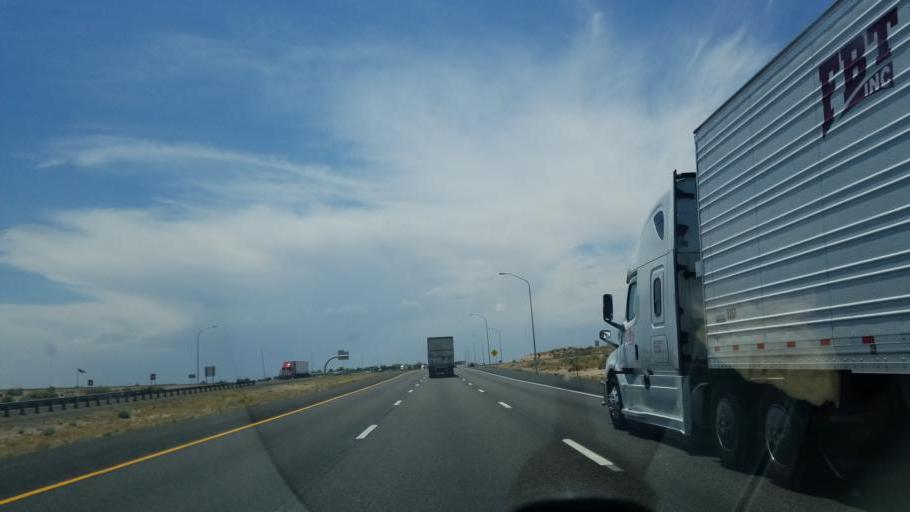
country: US
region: New Mexico
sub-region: Bernalillo County
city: South Valley
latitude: 35.0649
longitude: -106.7884
